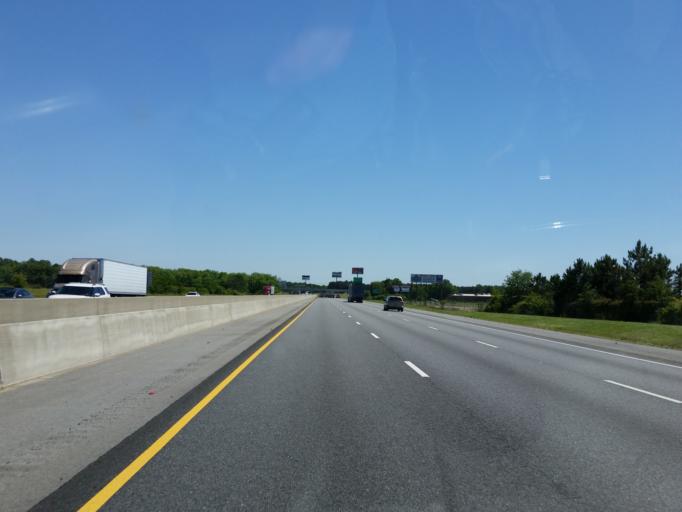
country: US
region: Georgia
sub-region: Turner County
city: Ashburn
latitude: 31.6995
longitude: -83.6320
